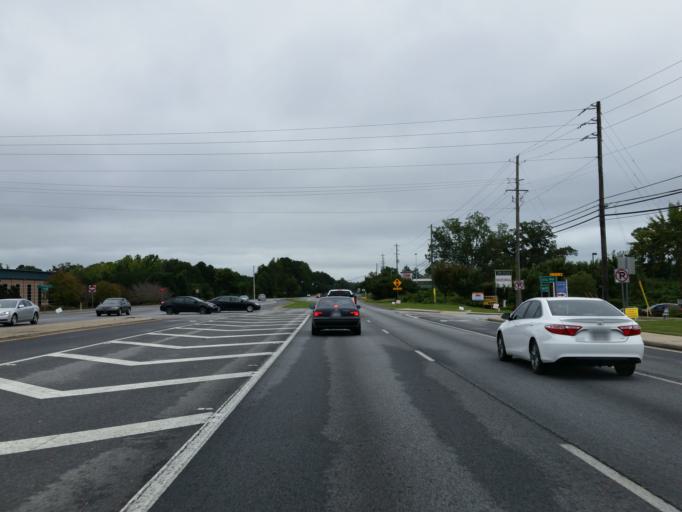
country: US
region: Georgia
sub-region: Clayton County
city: Bonanza
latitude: 33.4765
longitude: -84.3377
